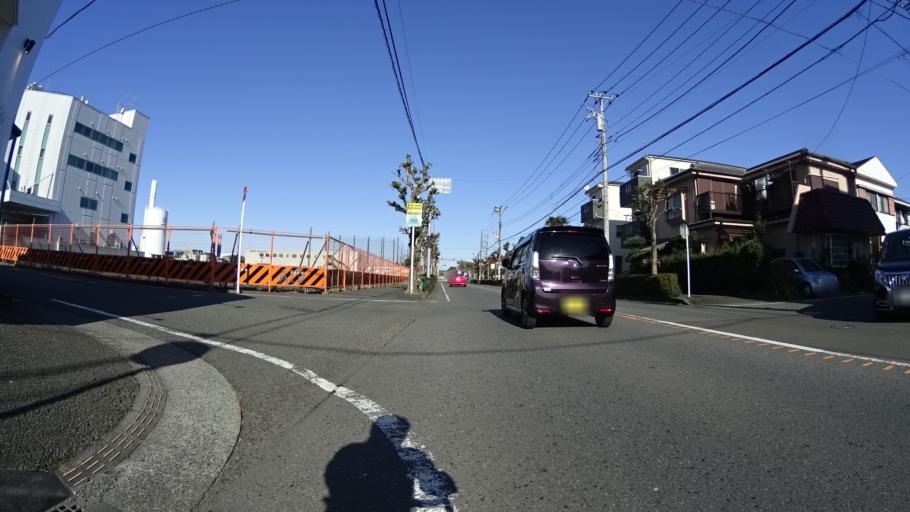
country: JP
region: Tokyo
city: Hachioji
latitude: 35.5829
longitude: 139.3621
